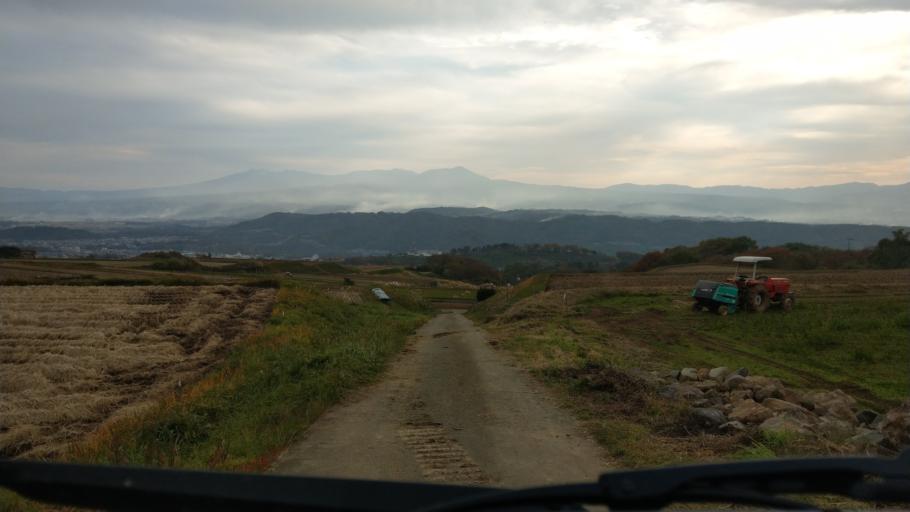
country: JP
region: Nagano
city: Komoro
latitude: 36.3568
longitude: 138.4263
